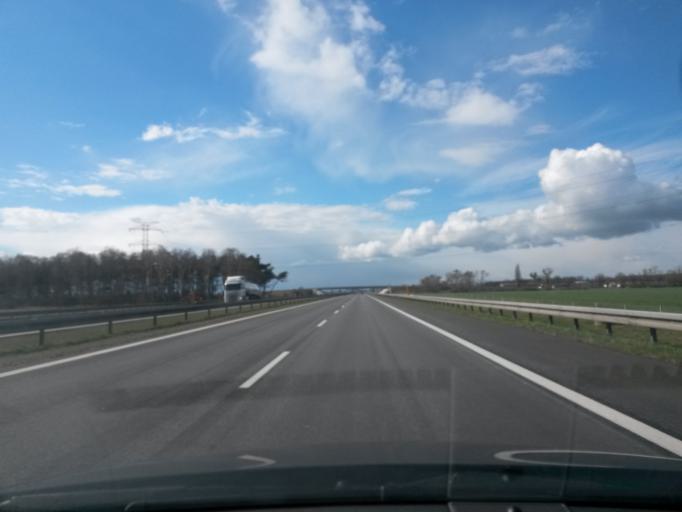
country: PL
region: Greater Poland Voivodeship
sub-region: Powiat wrzesinski
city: Kolaczkowo
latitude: 52.2798
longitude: 17.6954
